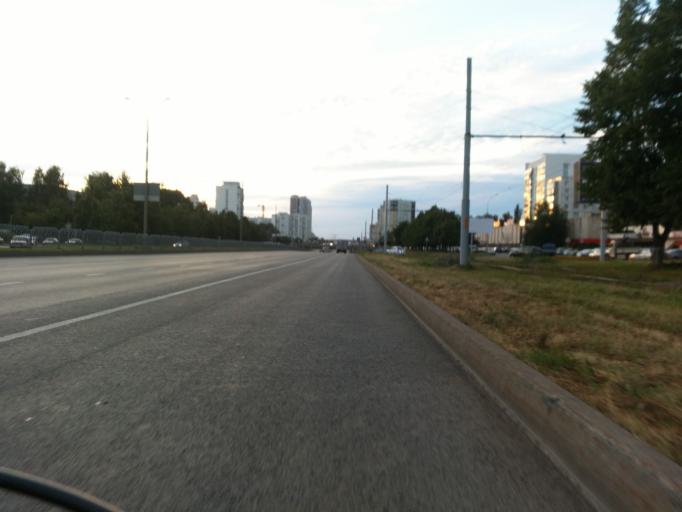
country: RU
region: Tatarstan
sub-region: Tukayevskiy Rayon
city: Naberezhnyye Chelny
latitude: 55.7466
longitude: 52.4223
